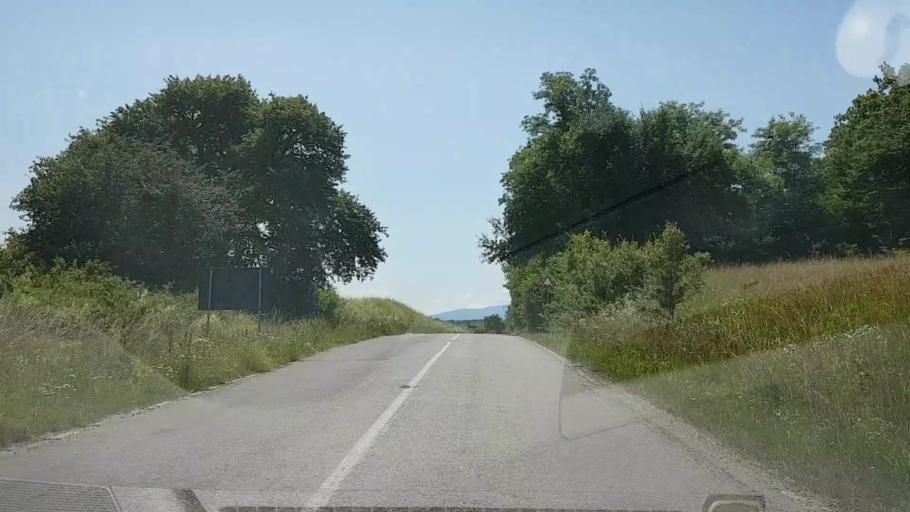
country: RO
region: Brasov
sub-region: Comuna Cincu
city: Cincu
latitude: 45.8694
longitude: 24.8225
